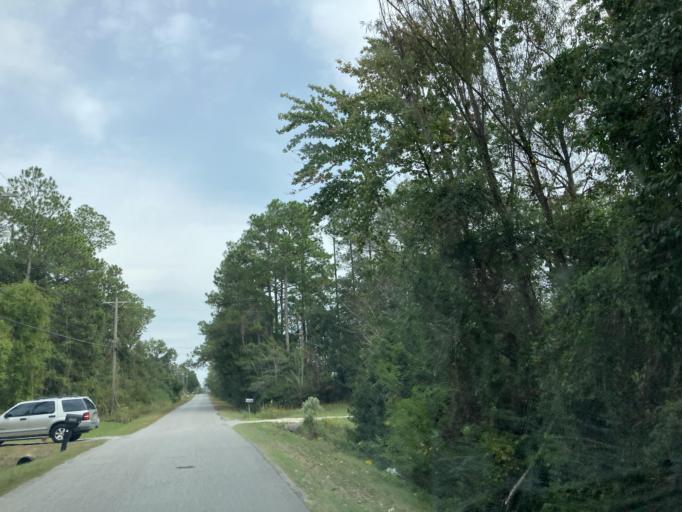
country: US
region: Mississippi
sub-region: Jackson County
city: Saint Martin
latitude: 30.4648
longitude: -88.8587
